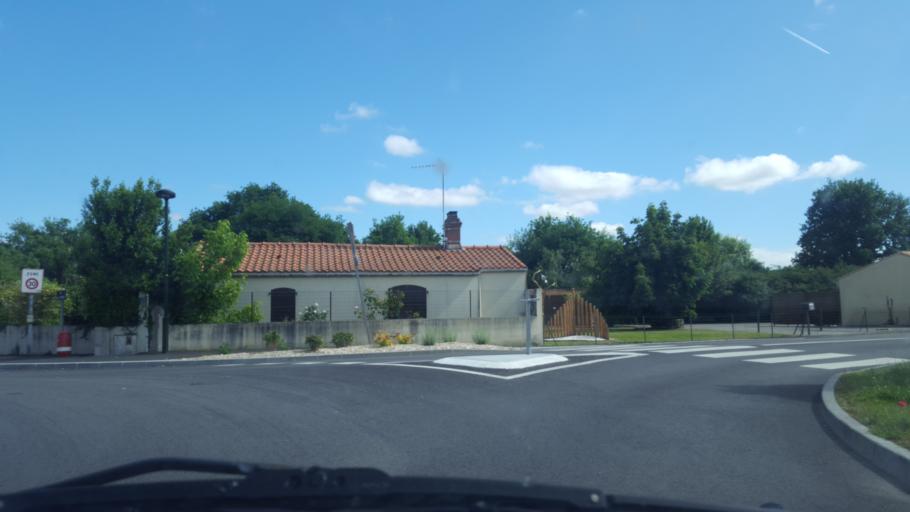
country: FR
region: Pays de la Loire
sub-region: Departement de la Loire-Atlantique
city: Paulx
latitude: 46.9972
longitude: -1.7369
